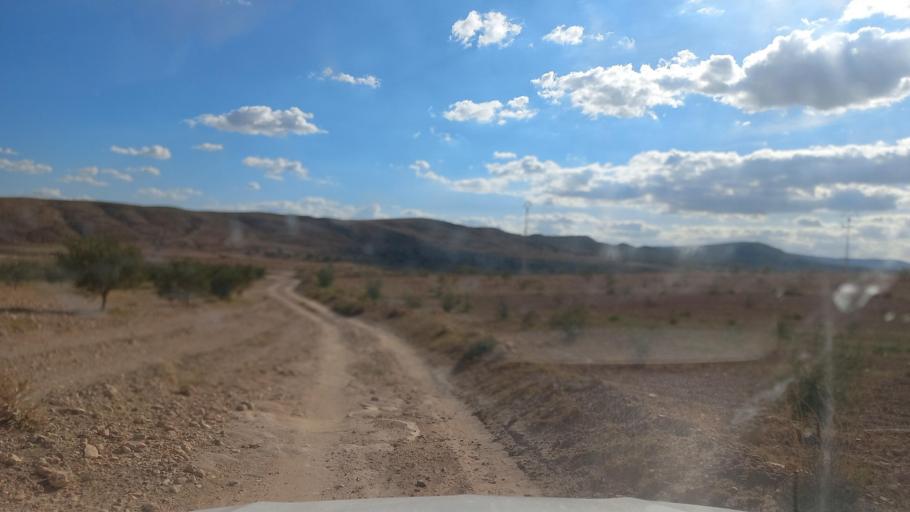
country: TN
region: Al Qasrayn
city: Sbiba
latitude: 35.3966
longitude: 9.0152
